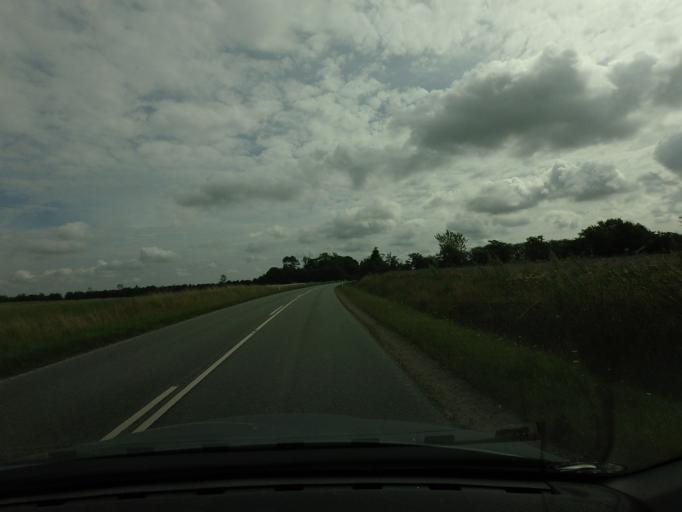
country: DK
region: North Denmark
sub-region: Bronderslev Kommune
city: Dronninglund
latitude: 57.2871
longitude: 10.3045
